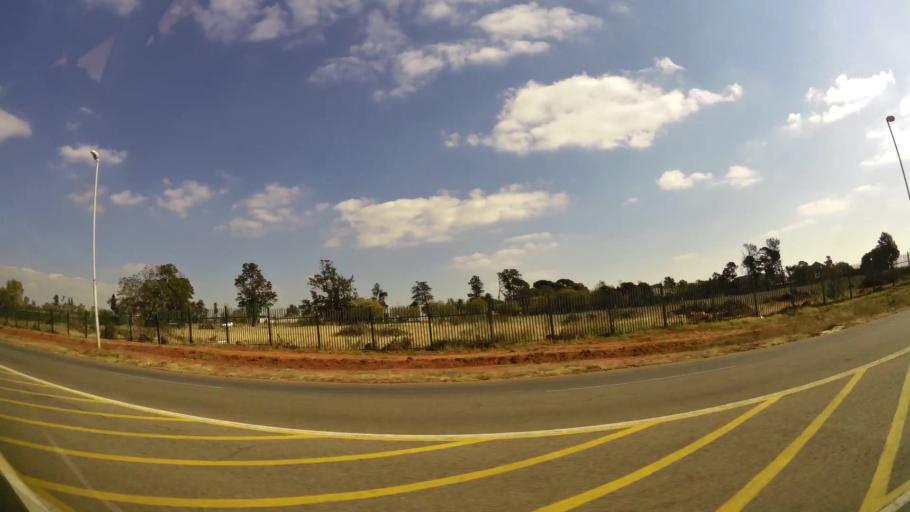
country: ZA
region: Gauteng
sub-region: West Rand District Municipality
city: Krugersdorp
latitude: -26.0581
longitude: 27.7559
